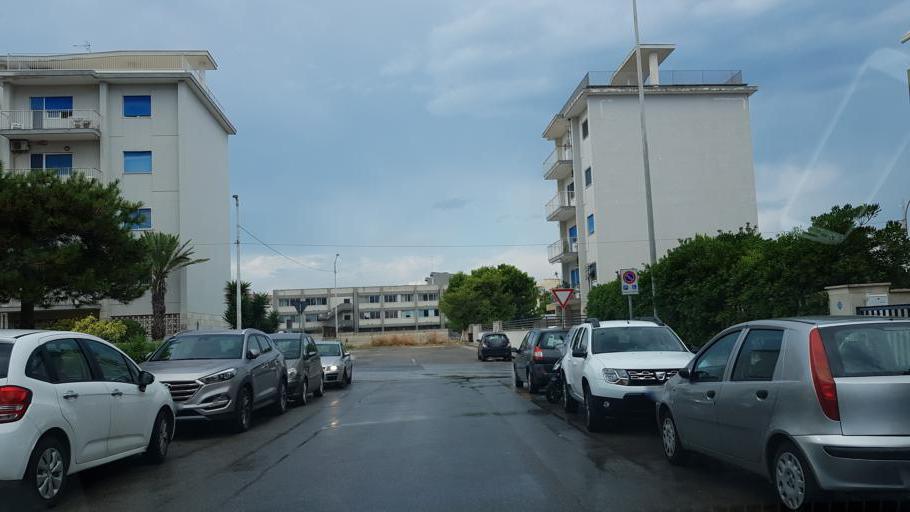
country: IT
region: Apulia
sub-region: Provincia di Bari
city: Monopoli
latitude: 40.9453
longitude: 17.3075
